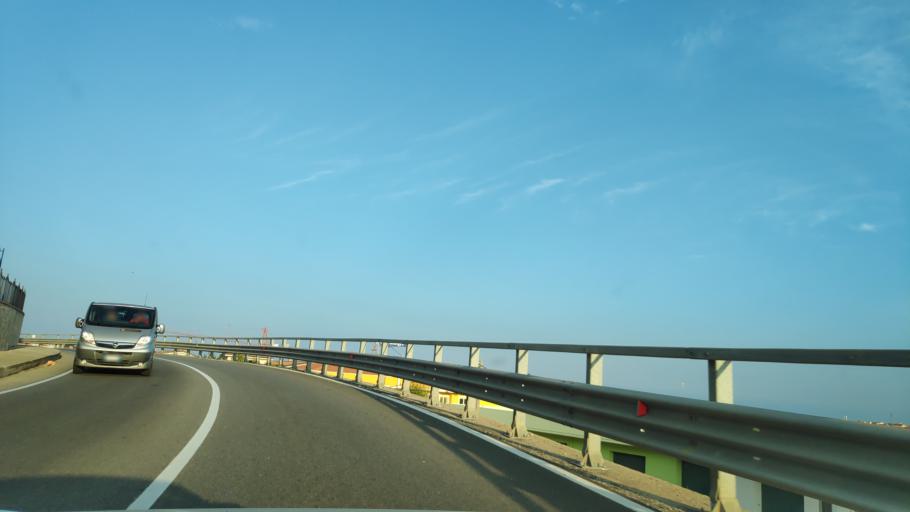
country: IT
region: Calabria
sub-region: Provincia di Catanzaro
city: Martelli-Laganosa
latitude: 38.6788
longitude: 16.5373
